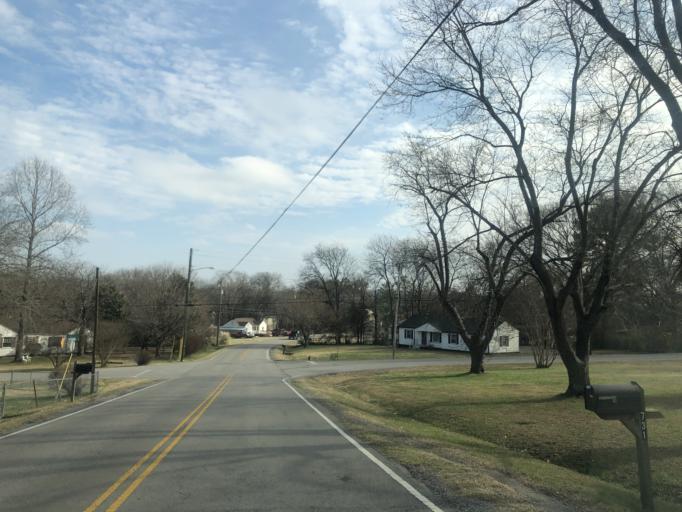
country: US
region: Tennessee
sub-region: Davidson County
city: Oak Hill
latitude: 36.1125
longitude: -86.7146
